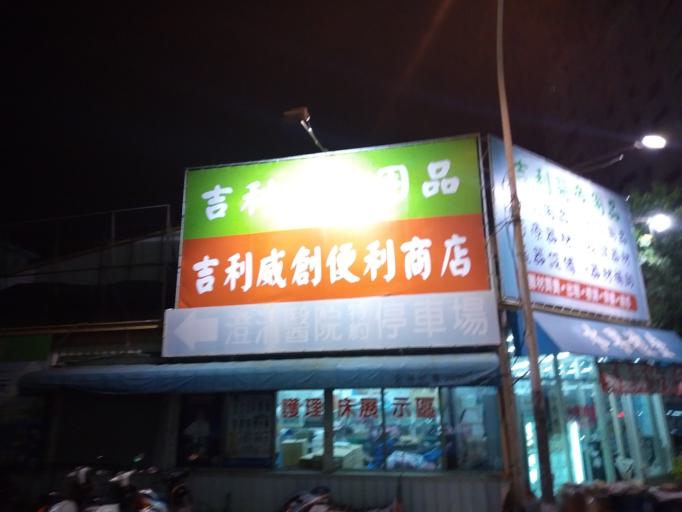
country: TW
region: Taiwan
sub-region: Taichung City
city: Taichung
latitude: 24.1833
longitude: 120.6169
